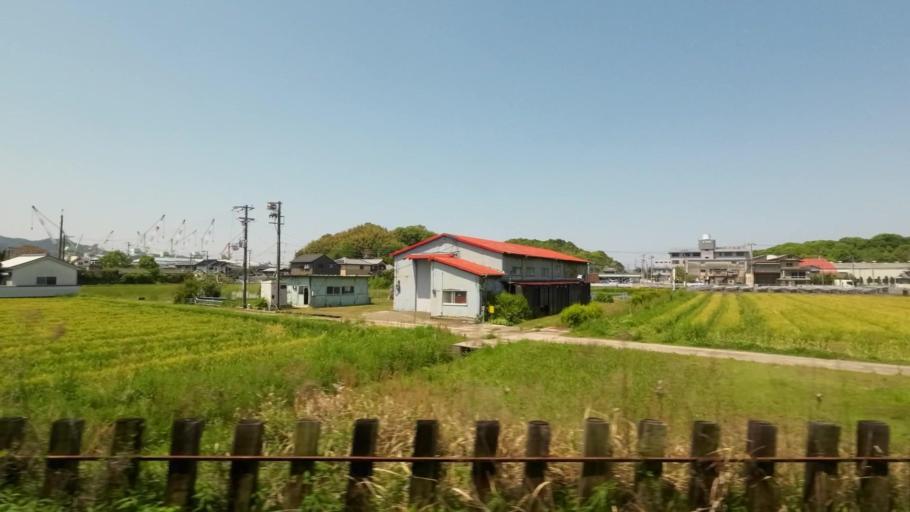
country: JP
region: Ehime
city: Hojo
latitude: 34.0753
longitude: 132.9315
